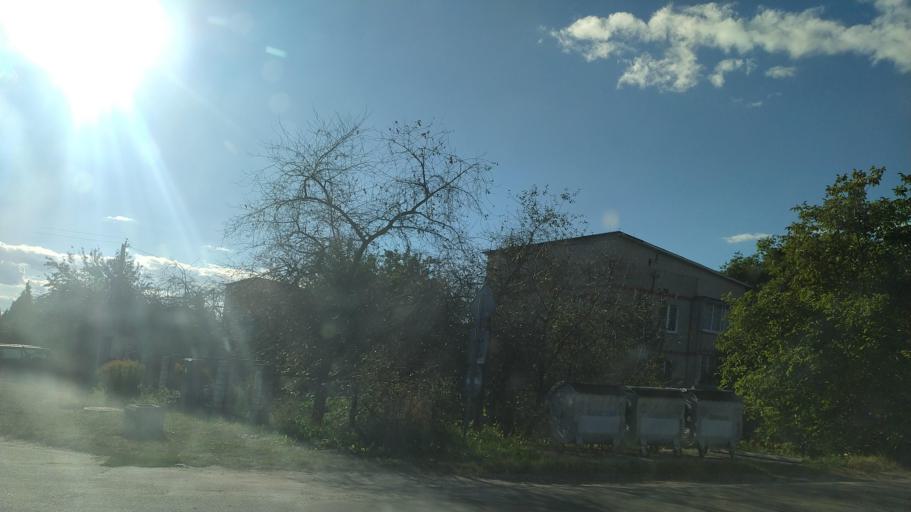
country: BY
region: Brest
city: Byaroza
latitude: 52.5463
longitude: 24.9743
